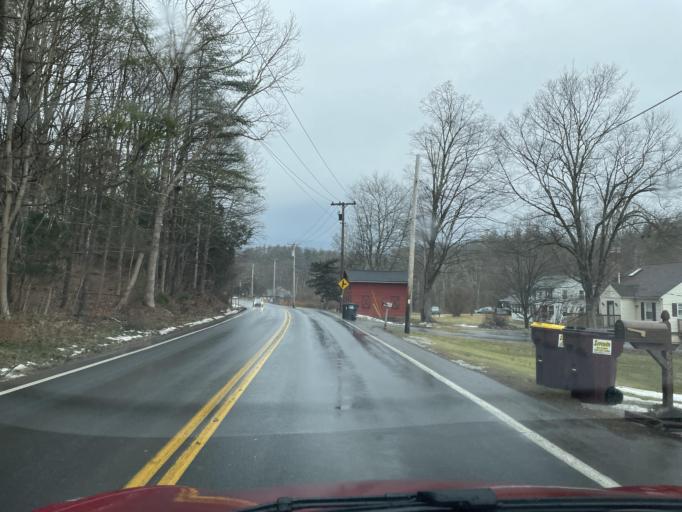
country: US
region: New York
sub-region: Ulster County
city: Saugerties
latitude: 42.0820
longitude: -73.9983
